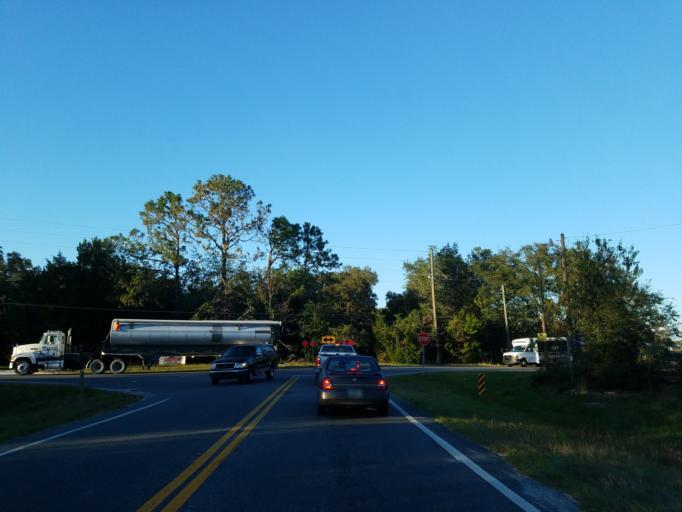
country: US
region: Florida
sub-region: Sumter County
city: Bushnell
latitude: 28.6402
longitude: -82.2034
